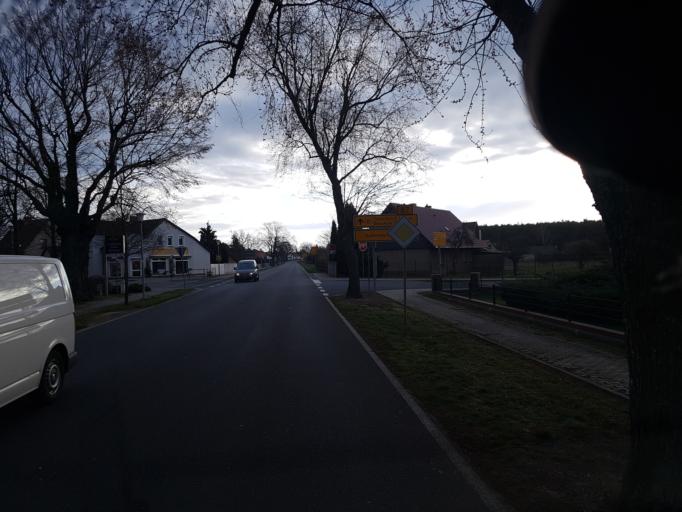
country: DE
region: Brandenburg
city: Schlepzig
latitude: 51.9851
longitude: 13.9733
